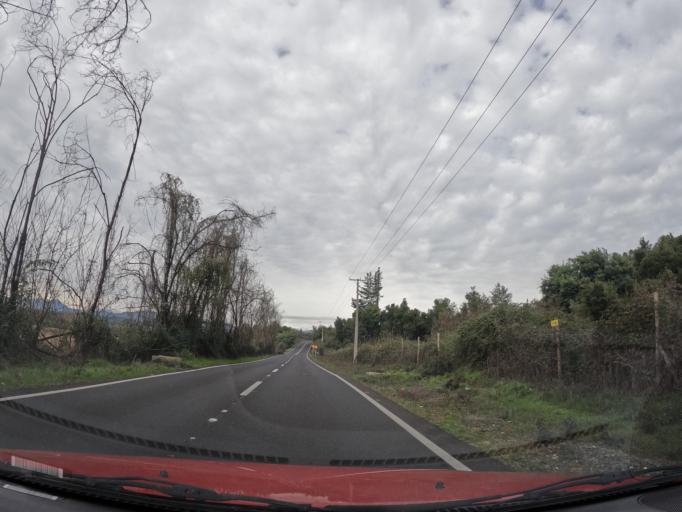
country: CL
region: Maule
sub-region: Provincia de Linares
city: Linares
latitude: -35.9137
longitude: -71.4748
